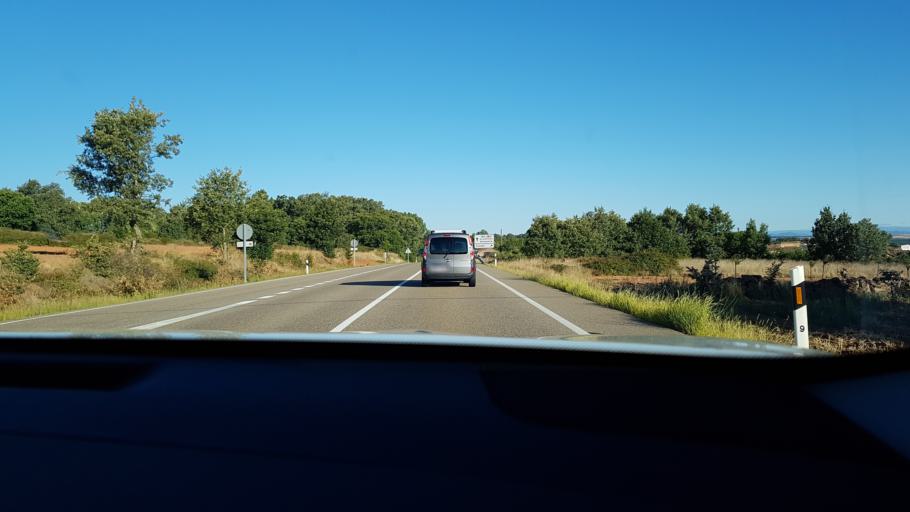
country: ES
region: Castille and Leon
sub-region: Provincia de Zamora
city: Rabanales
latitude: 41.6795
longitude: -6.2500
